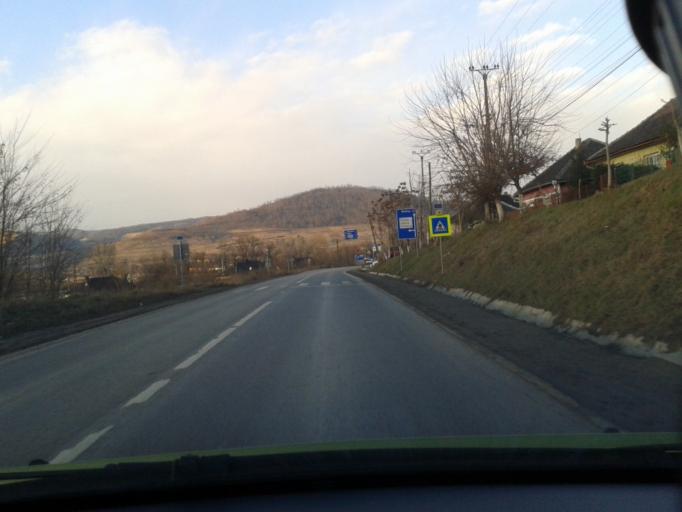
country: RO
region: Sibiu
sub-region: Comuna Tarnava
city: Tarnava
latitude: 46.1310
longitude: 24.2989
